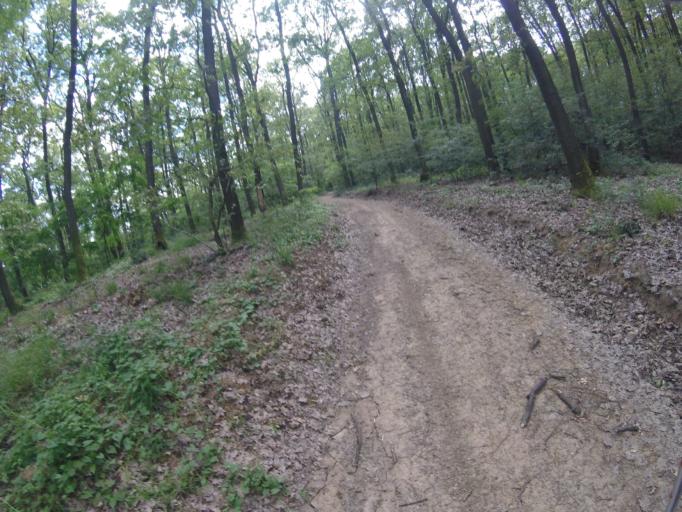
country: HU
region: Nograd
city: Romhany
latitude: 47.8916
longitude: 19.2709
